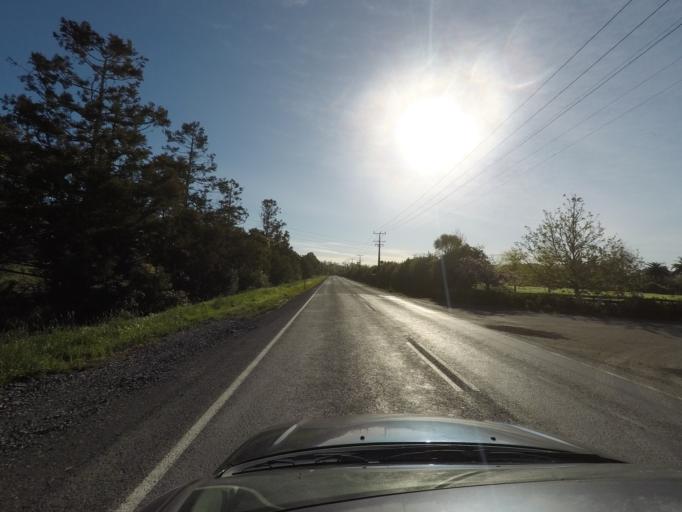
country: NZ
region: Auckland
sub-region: Auckland
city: Red Hill
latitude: -37.0003
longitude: 174.9636
